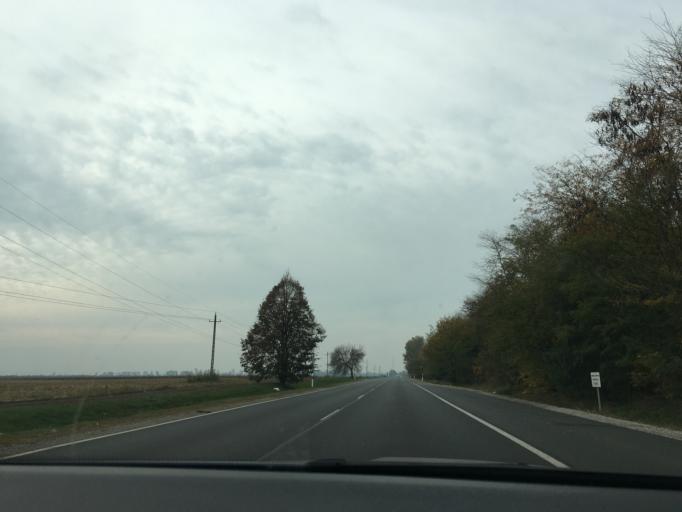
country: HU
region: Hajdu-Bihar
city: Puspokladany
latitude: 47.3415
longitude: 21.1753
